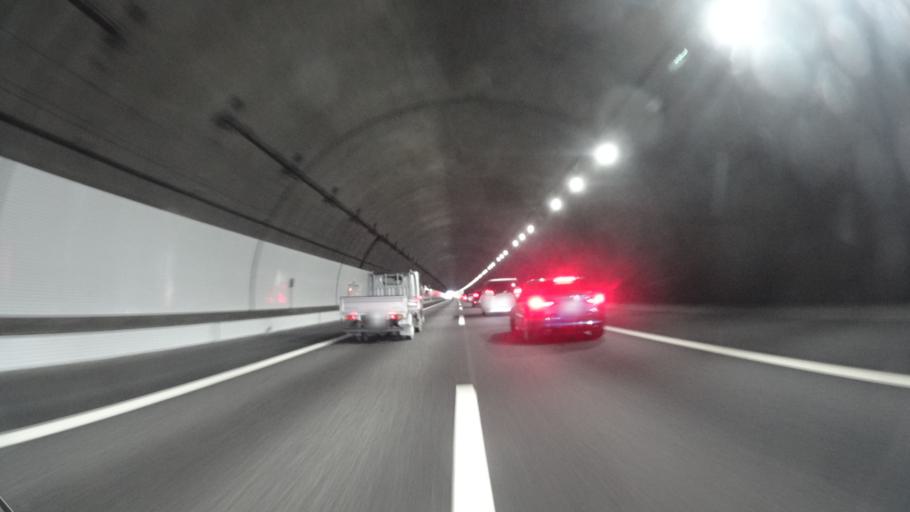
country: JP
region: Shiga Prefecture
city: Minakuchicho-matoba
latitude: 34.9221
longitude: 136.1162
